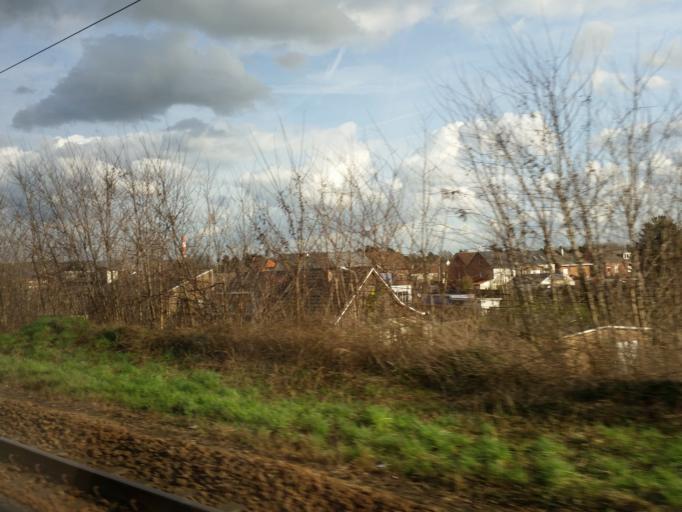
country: BE
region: Flanders
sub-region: Provincie Vlaams-Brabant
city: Kapelle-op-den-Bos
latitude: 51.0106
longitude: 4.3556
